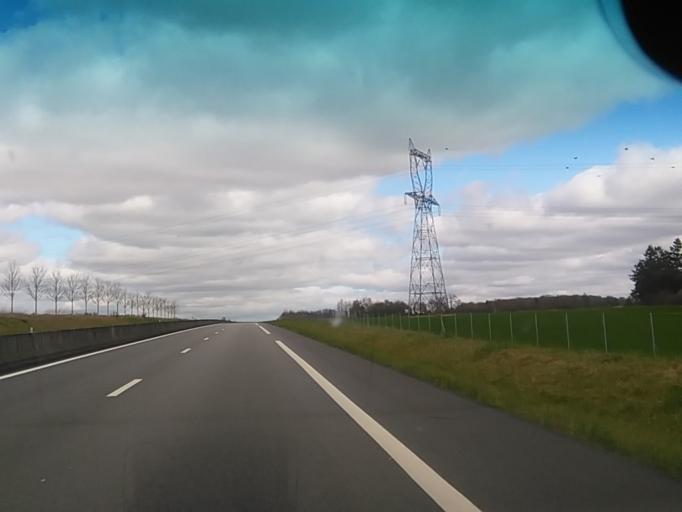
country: FR
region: Haute-Normandie
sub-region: Departement de l'Eure
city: Bourg-Achard
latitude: 49.2903
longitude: 0.7857
